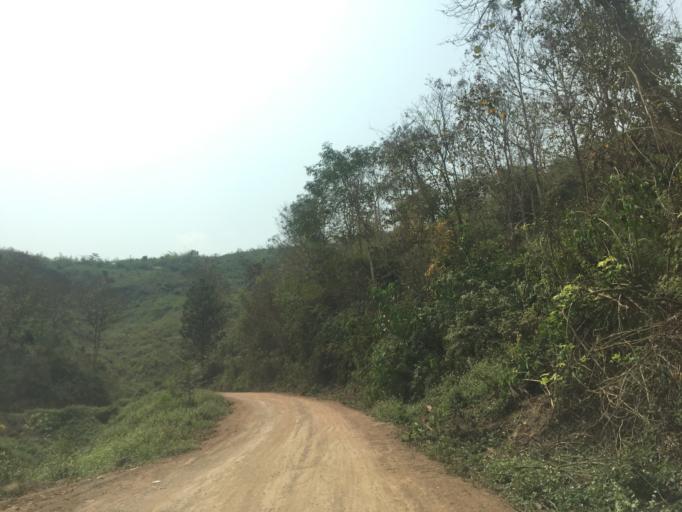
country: LA
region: Loungnamtha
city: Muang Nale
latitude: 20.3015
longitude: 101.6589
